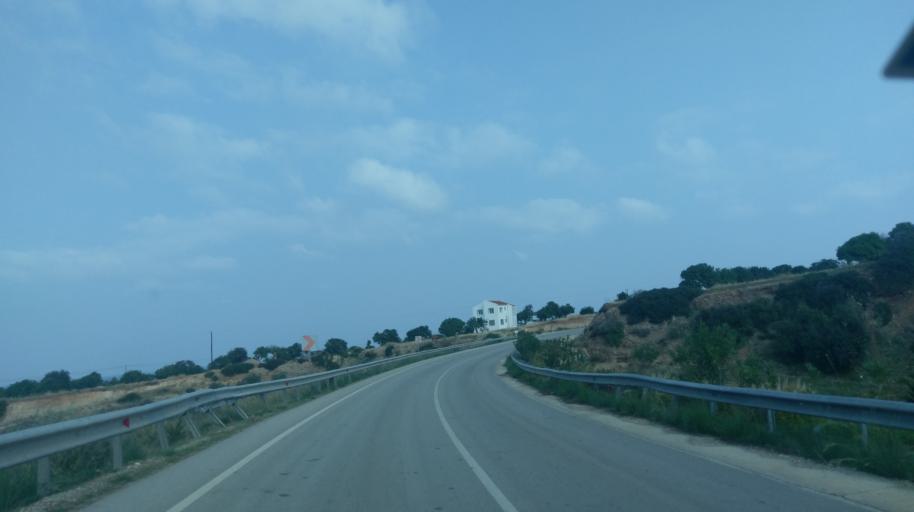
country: CY
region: Ammochostos
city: Lefkonoiko
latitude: 35.3824
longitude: 33.7198
